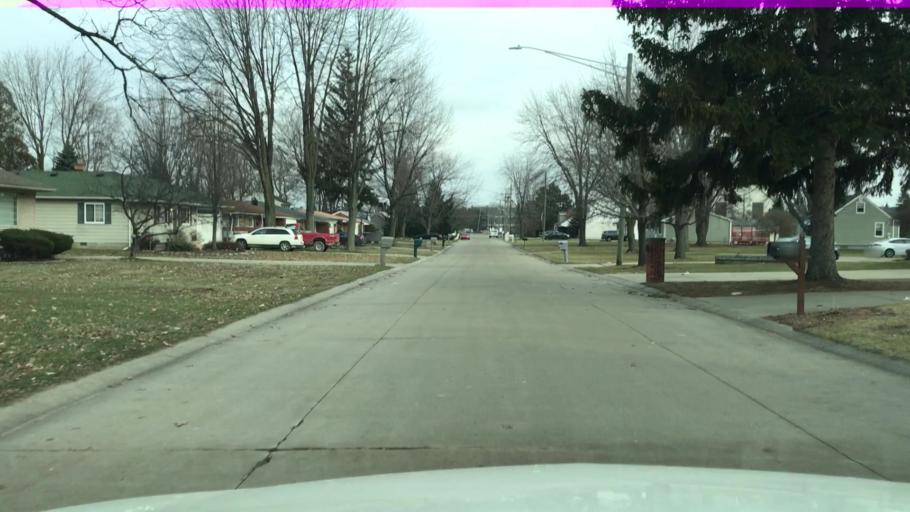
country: US
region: Michigan
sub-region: Macomb County
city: Sterling Heights
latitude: 42.5638
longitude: -83.0530
